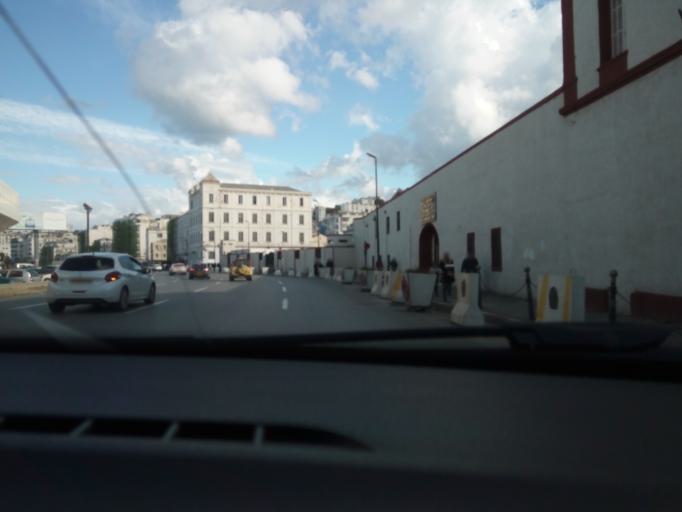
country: DZ
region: Alger
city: Algiers
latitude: 36.7954
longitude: 3.0514
